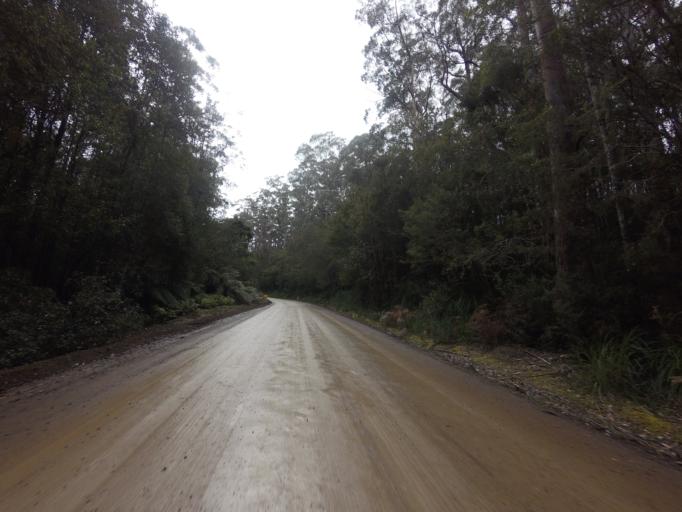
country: AU
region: Tasmania
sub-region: Huon Valley
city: Geeveston
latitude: -43.4154
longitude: 146.8755
